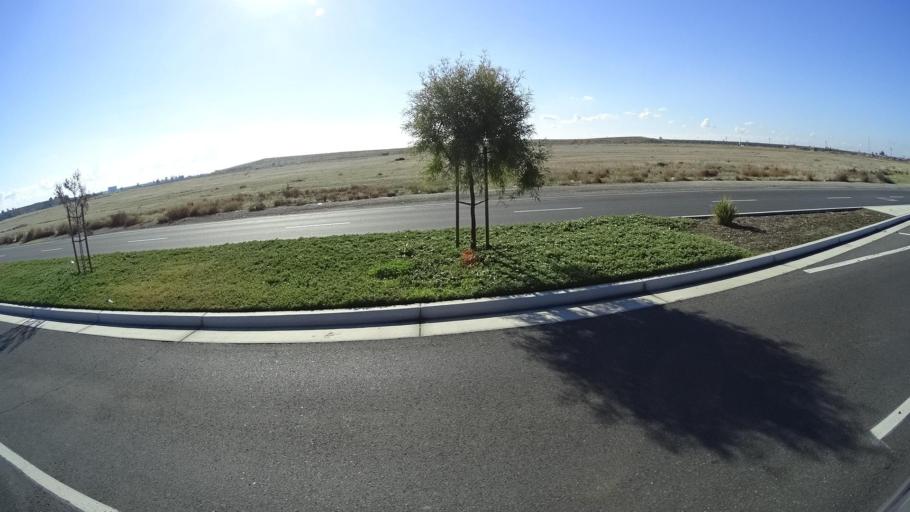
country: US
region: California
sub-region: Kern County
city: Delano
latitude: 35.7474
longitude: -119.2541
